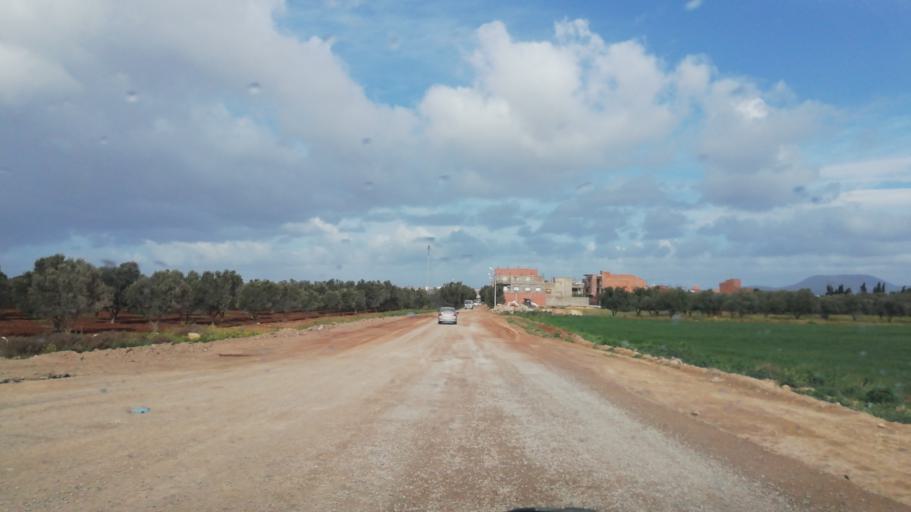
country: DZ
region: Oran
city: Sidi ech Chahmi
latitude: 35.6502
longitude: -0.5186
